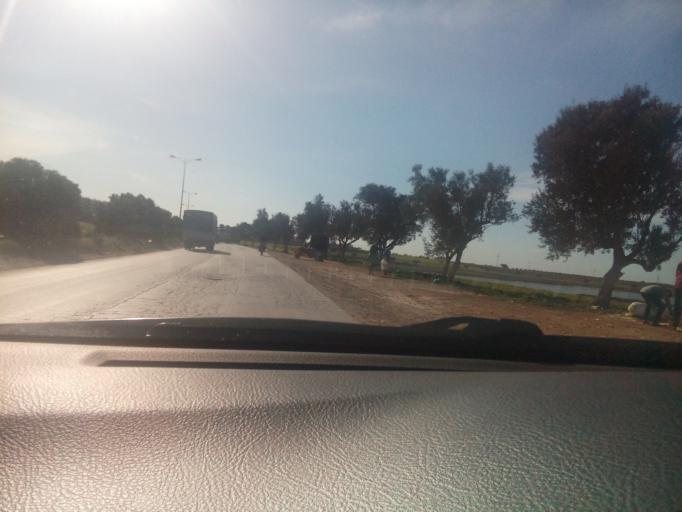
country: DZ
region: Oran
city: Sidi ech Chahmi
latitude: 35.6684
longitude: -0.5664
